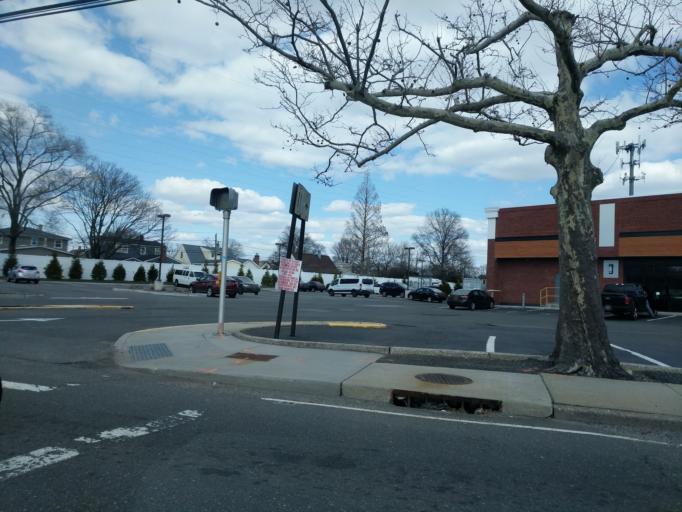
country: US
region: New York
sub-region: Nassau County
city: Hewlett
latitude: 40.6449
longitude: -73.7050
